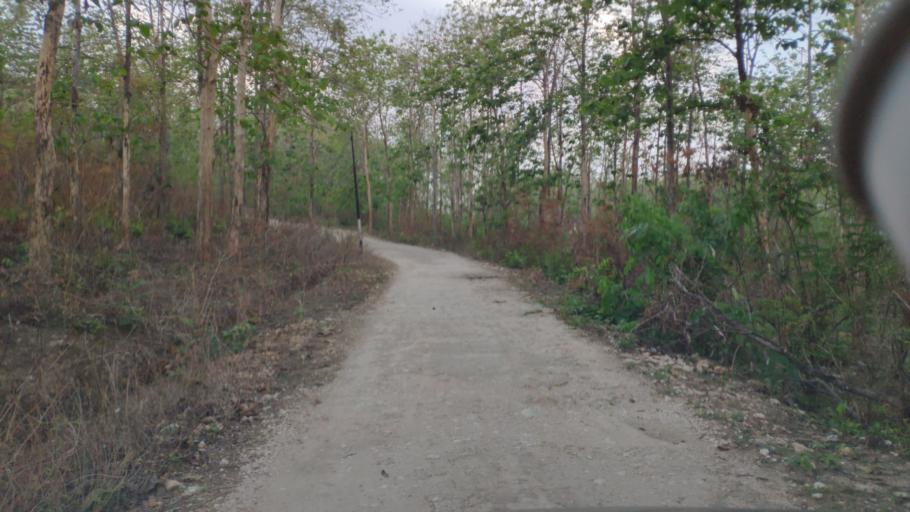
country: ID
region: Central Java
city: Semanggi
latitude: -7.0656
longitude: 111.4276
